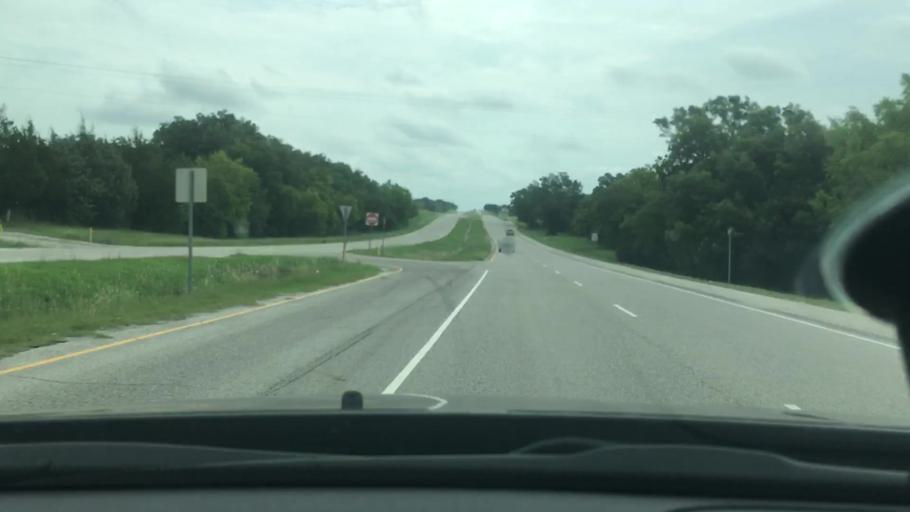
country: US
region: Oklahoma
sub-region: Carter County
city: Wilson
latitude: 34.1729
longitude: -97.4226
